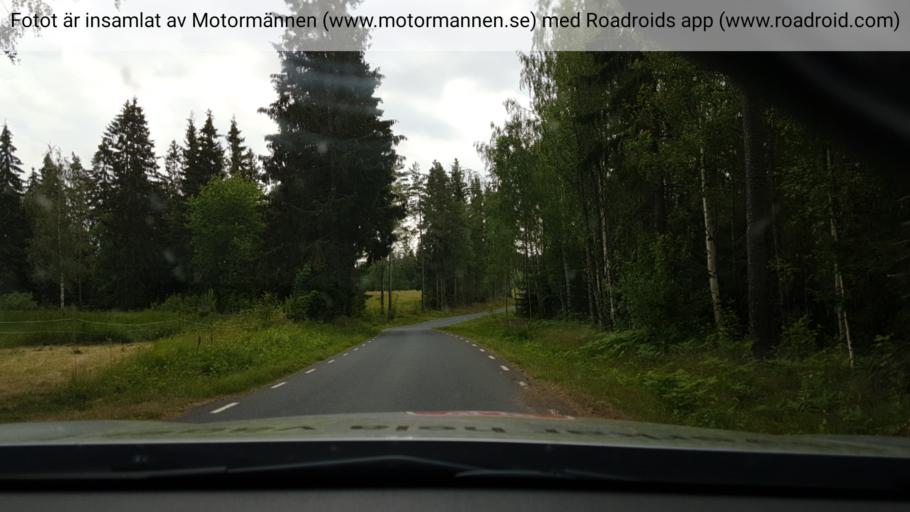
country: SE
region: Joenkoeping
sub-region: Habo Kommun
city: Habo
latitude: 57.9409
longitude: 14.0073
